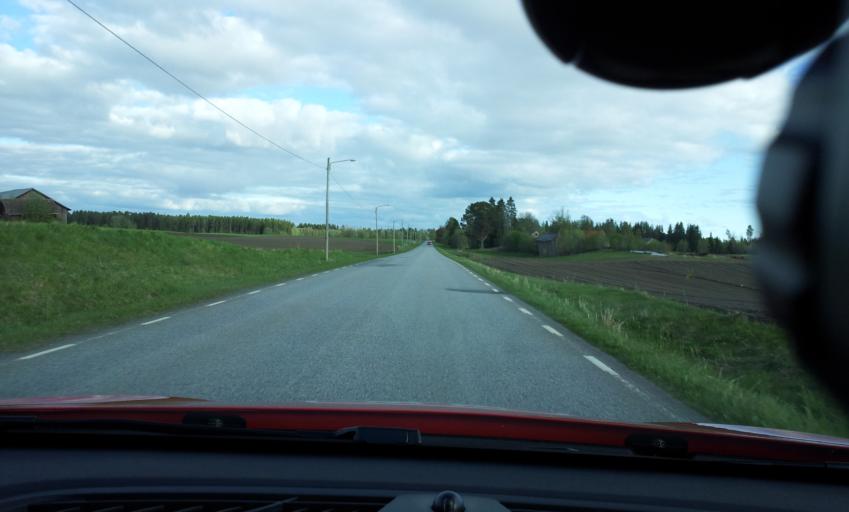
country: SE
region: Jaemtland
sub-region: Krokoms Kommun
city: Krokom
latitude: 63.2639
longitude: 14.3967
